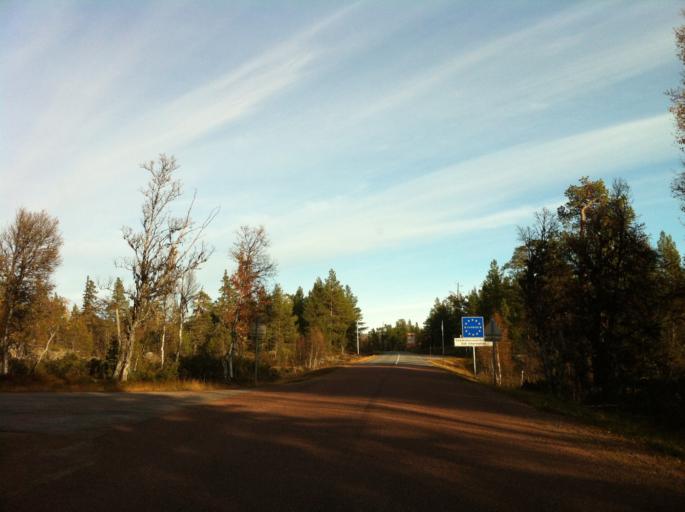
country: NO
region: Hedmark
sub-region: Engerdal
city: Engerdal
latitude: 62.0761
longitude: 12.1764
